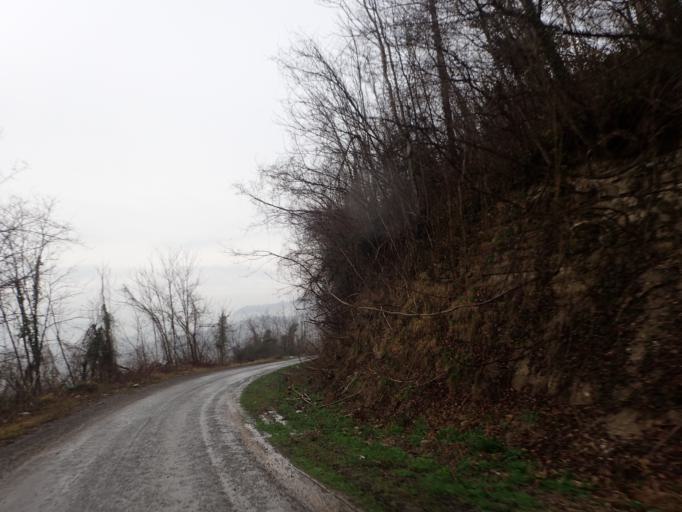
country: TR
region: Ordu
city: Camas
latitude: 40.9495
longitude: 37.5092
